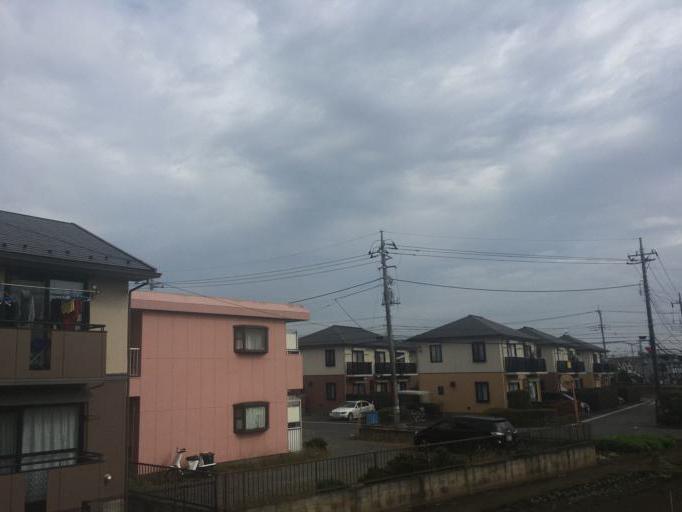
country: JP
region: Tokyo
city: Fussa
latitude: 35.7050
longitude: 139.3595
